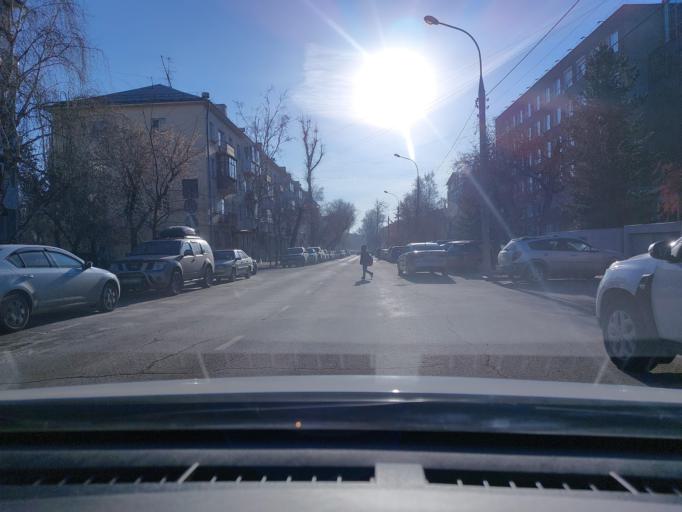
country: RU
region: Irkutsk
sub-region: Irkutskiy Rayon
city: Irkutsk
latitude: 52.2875
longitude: 104.2762
